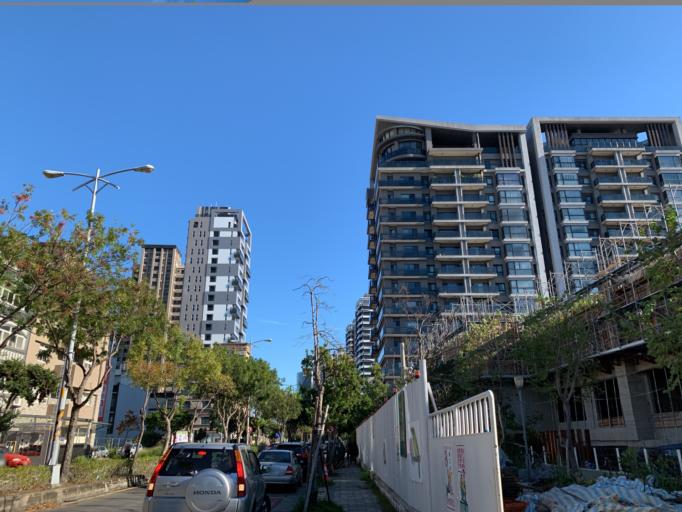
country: TW
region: Taiwan
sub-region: Hsinchu
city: Zhubei
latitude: 24.8113
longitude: 121.0313
